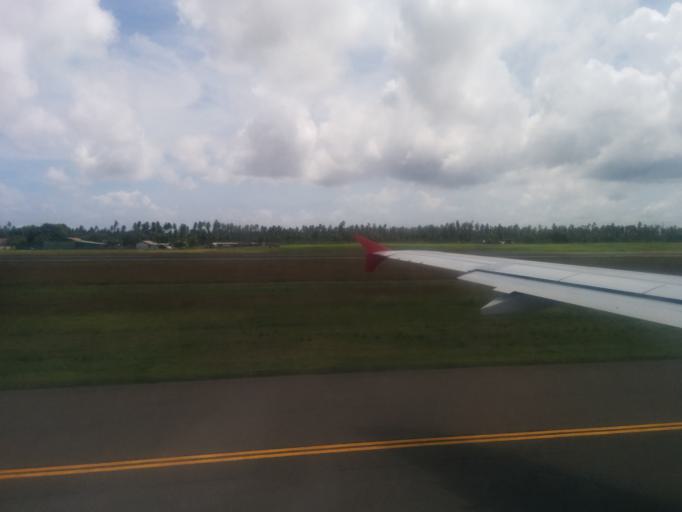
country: LK
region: Western
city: Katunayaka
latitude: 7.1828
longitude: 79.8874
